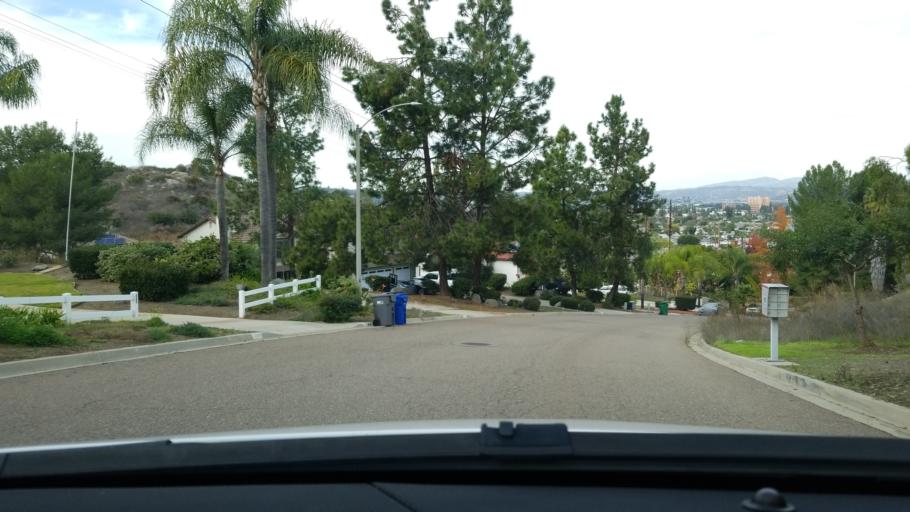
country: US
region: California
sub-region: San Diego County
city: Casa de Oro-Mount Helix
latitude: 32.7753
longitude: -116.9576
